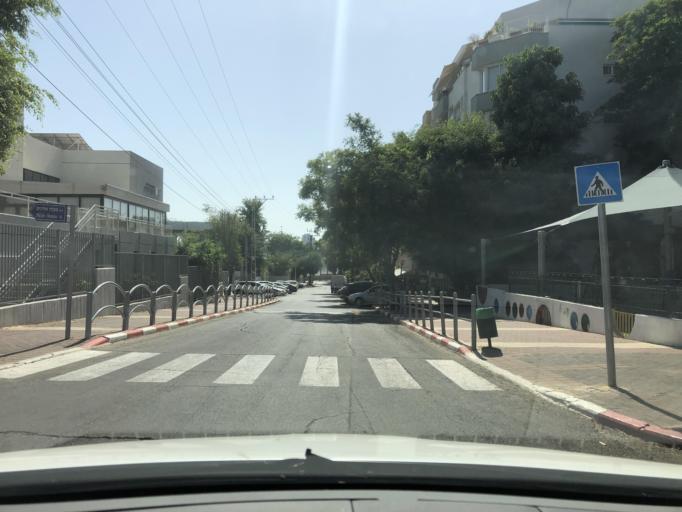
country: IL
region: Central District
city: Kfar Saba
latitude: 32.1737
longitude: 34.8963
